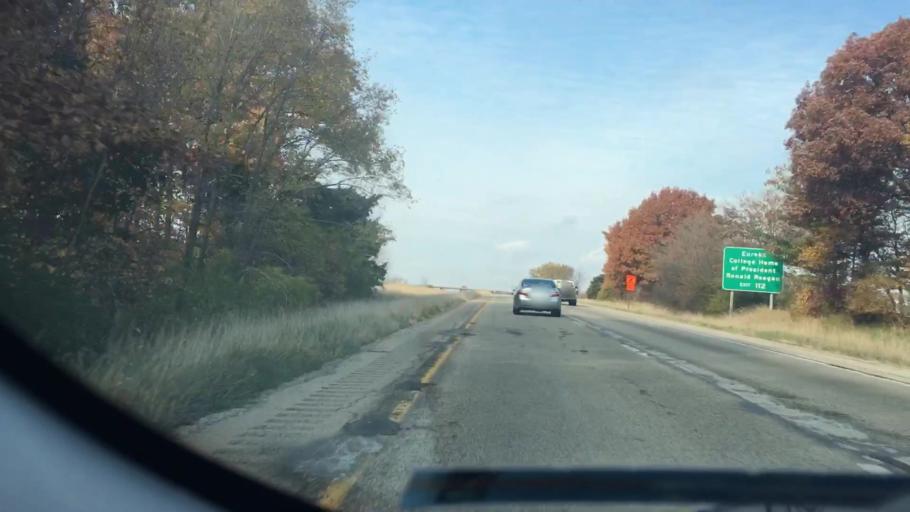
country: US
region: Illinois
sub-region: Woodford County
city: Eureka
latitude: 40.6196
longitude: -89.2649
